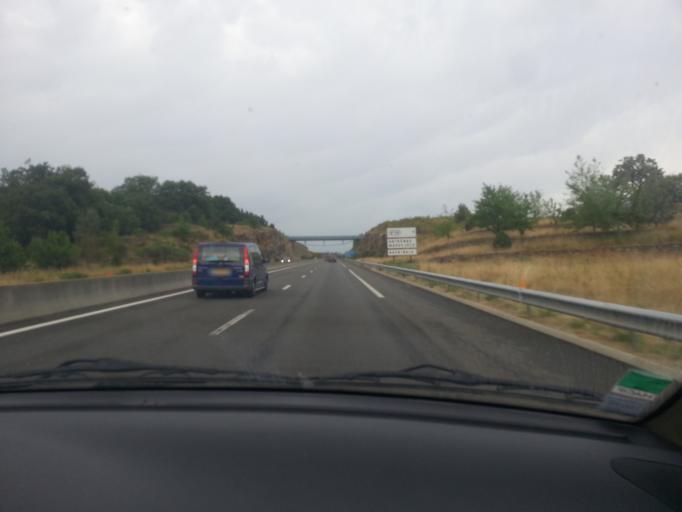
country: FR
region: Languedoc-Roussillon
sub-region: Departement de la Lozere
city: Chirac
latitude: 44.5177
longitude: 3.2411
